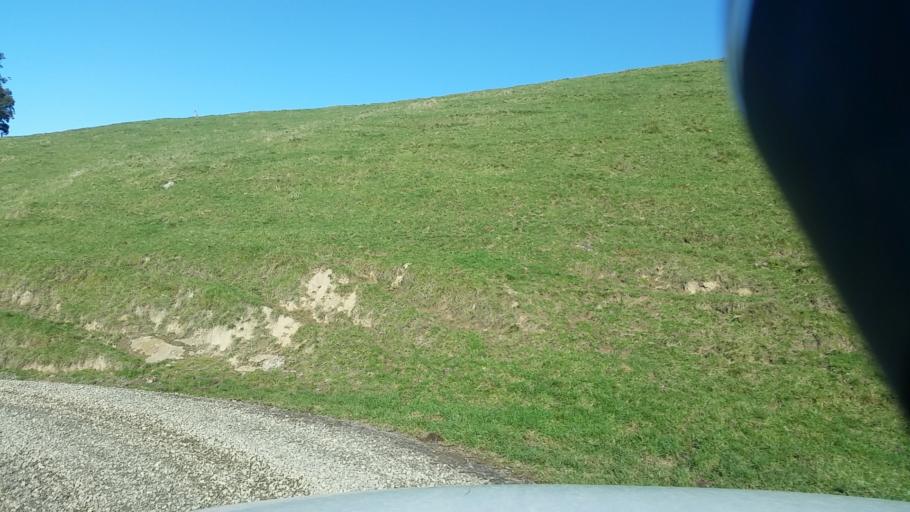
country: NZ
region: Canterbury
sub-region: Christchurch City
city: Christchurch
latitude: -43.6521
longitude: 172.9861
